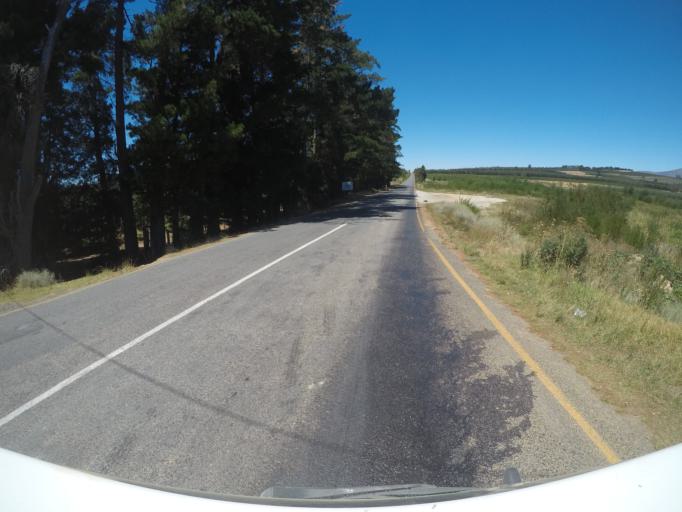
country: ZA
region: Western Cape
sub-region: Overberg District Municipality
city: Grabouw
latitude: -34.0542
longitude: 19.1484
